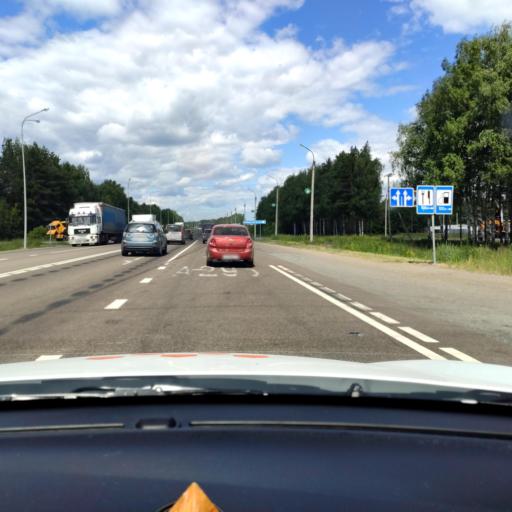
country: RU
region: Mariy-El
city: Volzhsk
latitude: 55.9155
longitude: 48.3681
